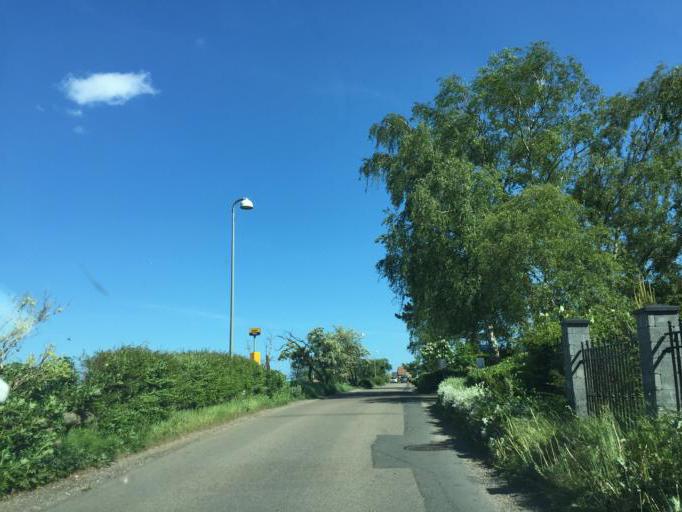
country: DK
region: Zealand
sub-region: Stevns Kommune
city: Stroby Egede
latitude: 55.4166
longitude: 12.2467
